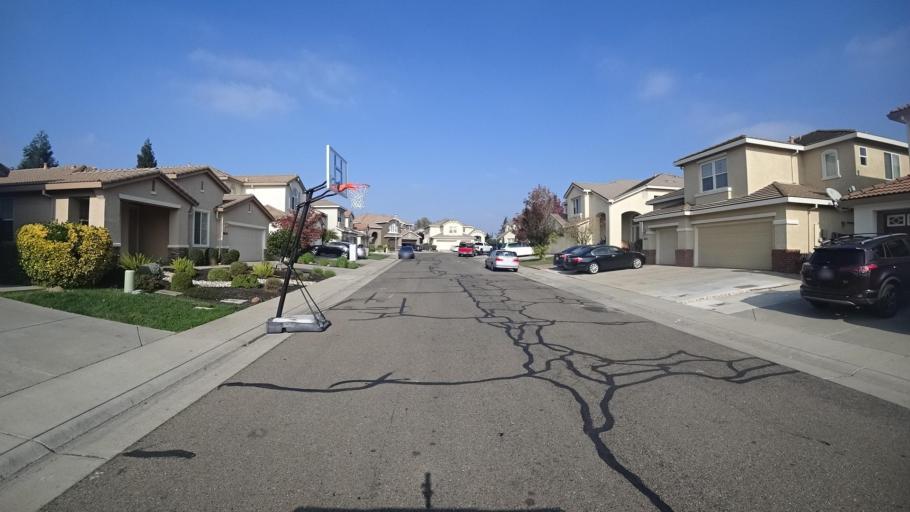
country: US
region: California
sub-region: Sacramento County
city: Vineyard
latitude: 38.4440
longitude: -121.3653
